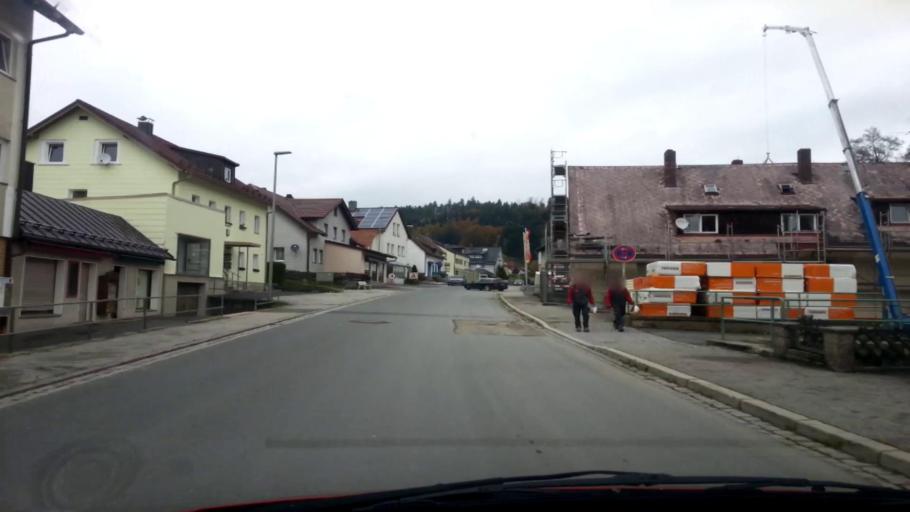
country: DE
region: Bavaria
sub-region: Upper Franconia
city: Warmensteinach
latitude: 49.9959
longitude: 11.7786
